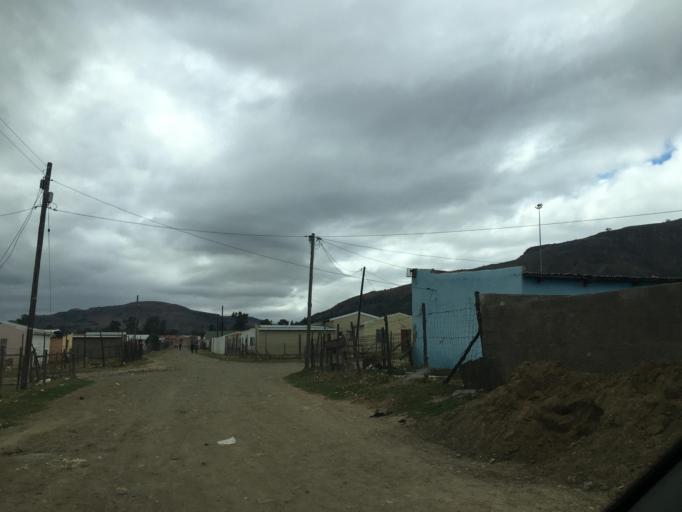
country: ZA
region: Eastern Cape
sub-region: Chris Hani District Municipality
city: Cala
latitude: -31.5343
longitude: 27.7003
